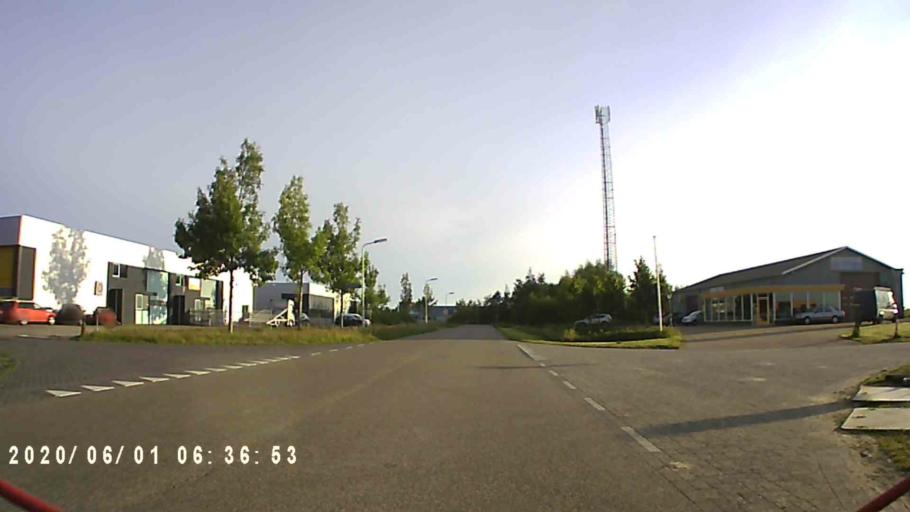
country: NL
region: Friesland
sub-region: Gemeente Kollumerland en Nieuwkruisland
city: Kollum
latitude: 53.2831
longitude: 6.1608
